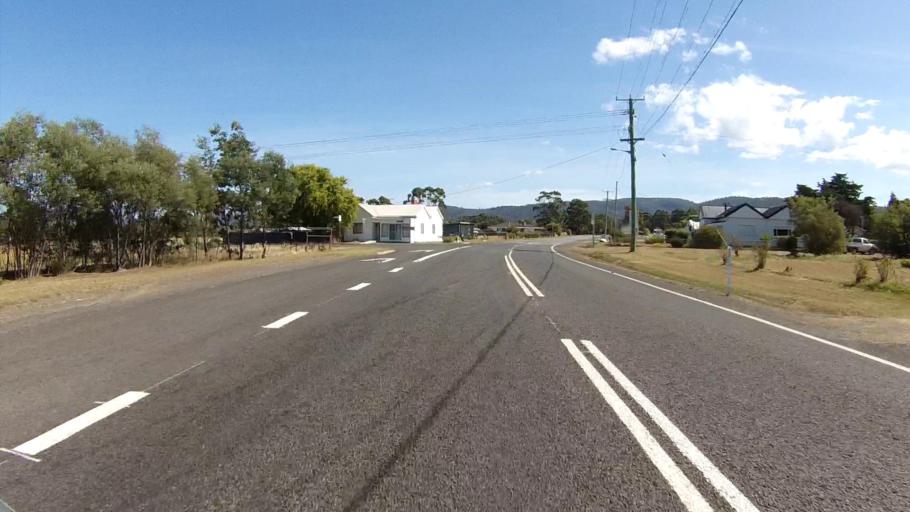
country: AU
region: Tasmania
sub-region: Sorell
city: Sorell
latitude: -42.5015
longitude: 147.9156
